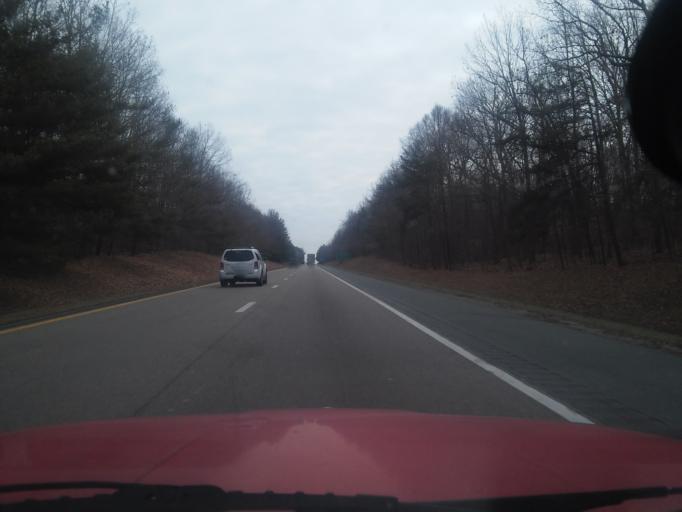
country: US
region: Virginia
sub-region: Louisa County
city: Louisa
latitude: 37.9467
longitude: -78.1246
